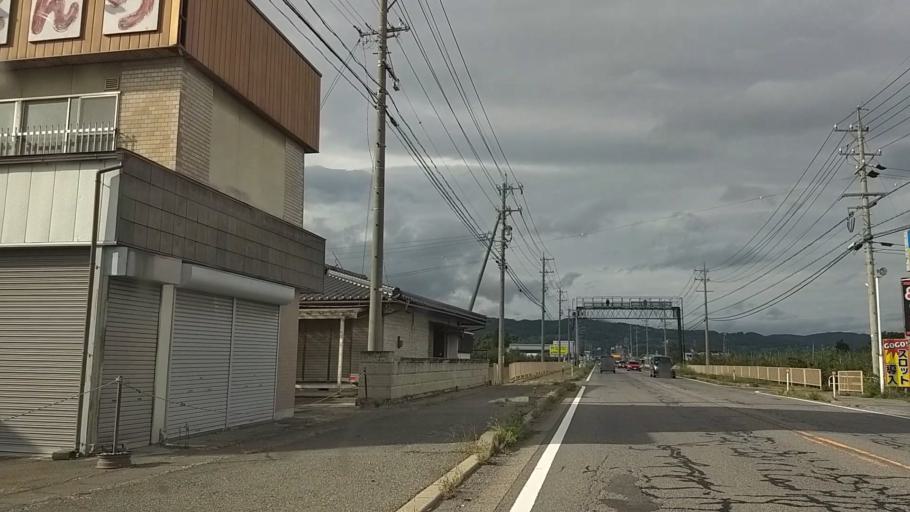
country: JP
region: Nagano
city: Suzaka
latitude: 36.6853
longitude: 138.2679
